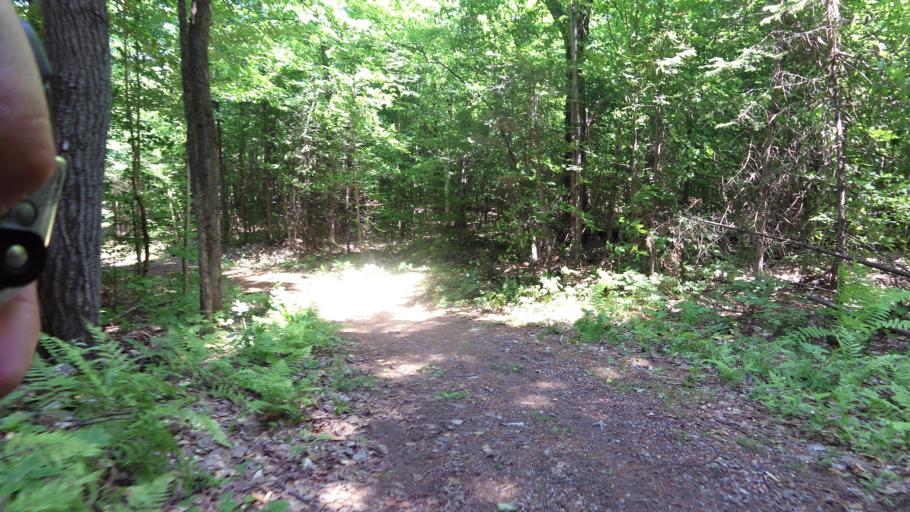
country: CA
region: Quebec
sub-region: Outaouais
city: Wakefield
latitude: 45.5934
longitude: -75.9670
